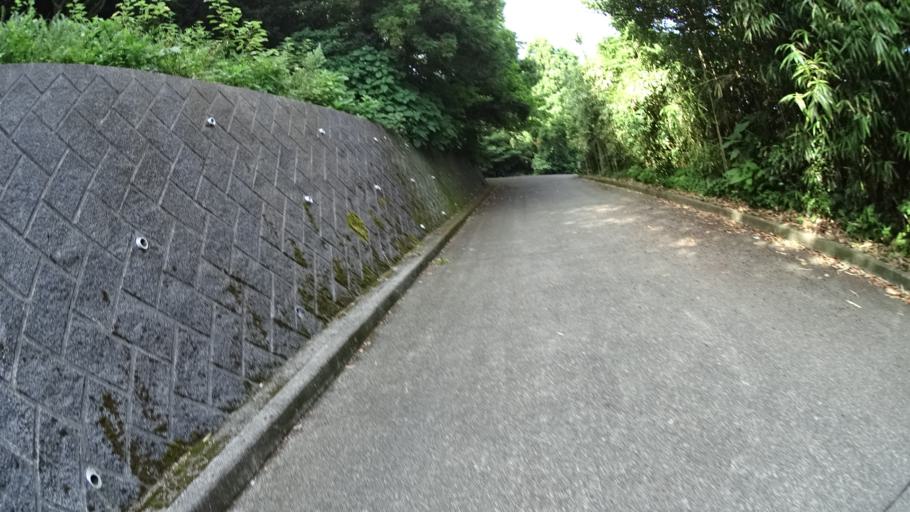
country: JP
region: Shizuoka
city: Shimoda
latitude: 34.5242
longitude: 139.2757
